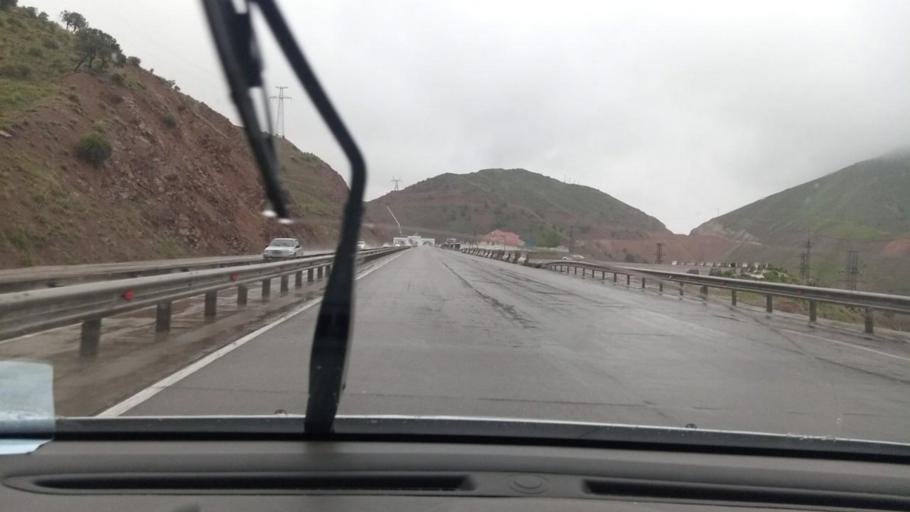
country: UZ
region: Toshkent
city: Angren
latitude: 41.0844
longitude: 70.5400
